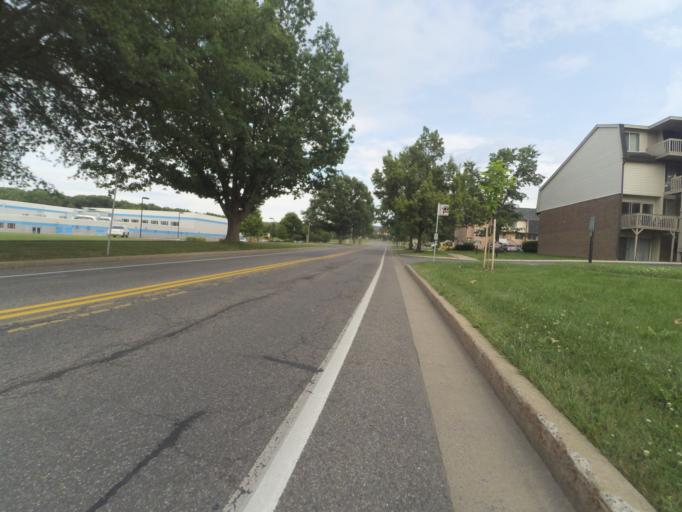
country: US
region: Pennsylvania
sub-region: Centre County
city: State College
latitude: 40.7740
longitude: -77.8560
